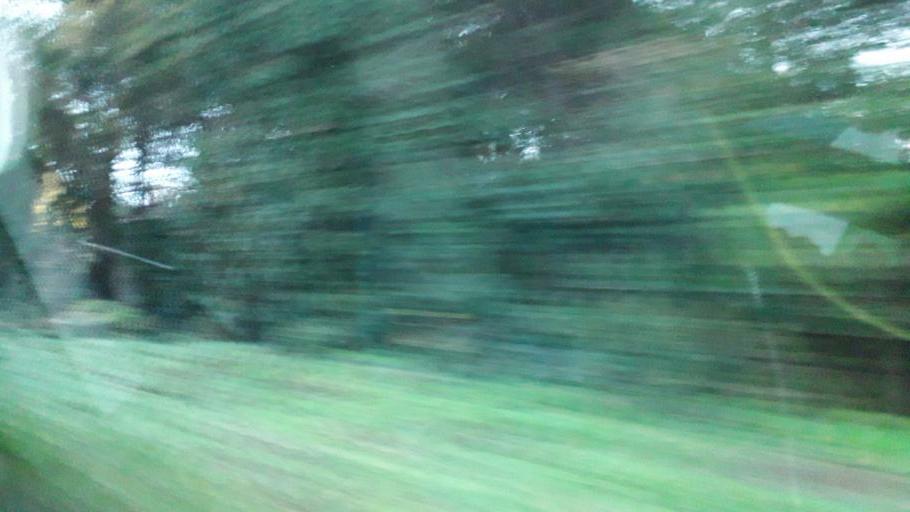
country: IE
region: Leinster
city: Malahide
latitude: 53.4370
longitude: -6.1769
